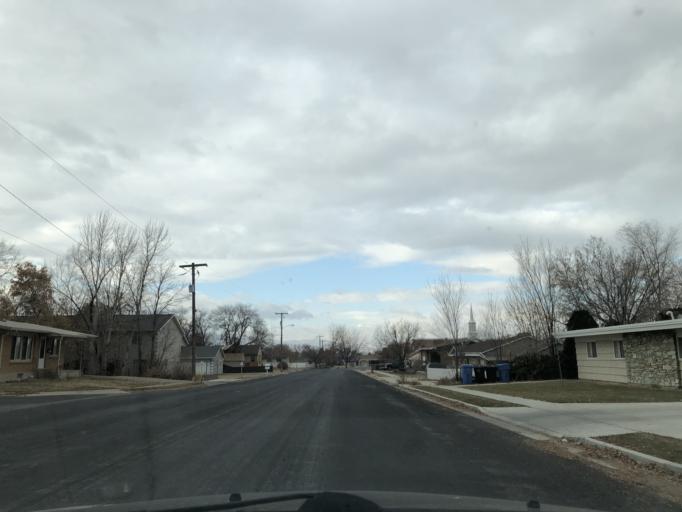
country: US
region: Utah
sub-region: Cache County
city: Logan
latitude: 41.7465
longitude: -111.8376
